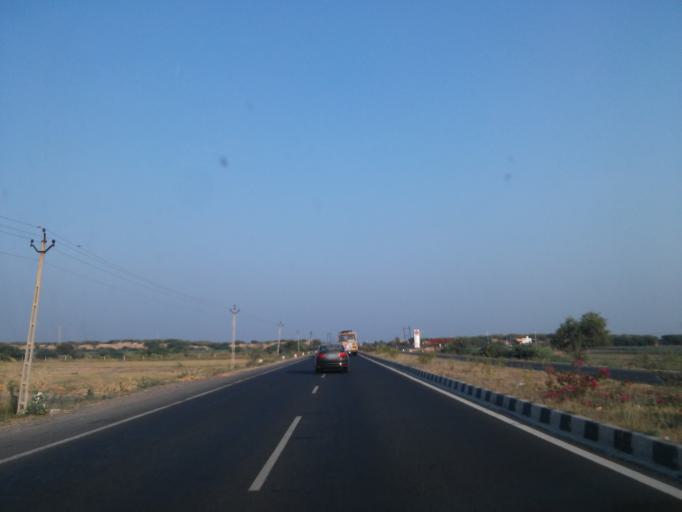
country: IN
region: Gujarat
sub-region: Ahmadabad
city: Mandal
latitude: 23.0979
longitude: 72.0867
